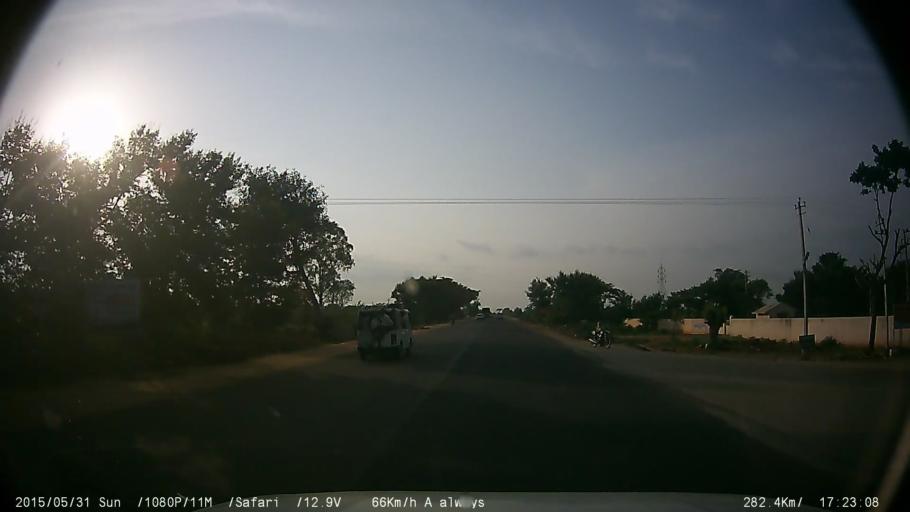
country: IN
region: Karnataka
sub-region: Chamrajnagar
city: Gundlupet
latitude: 11.8370
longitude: 76.6755
